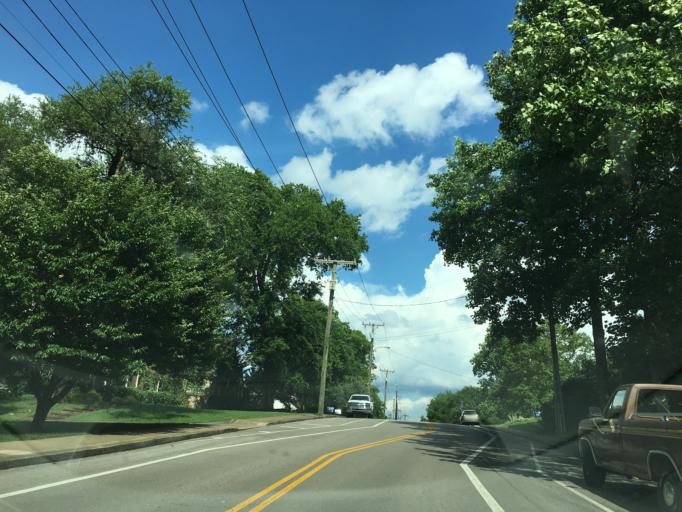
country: US
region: Tennessee
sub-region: Davidson County
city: Nashville
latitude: 36.1354
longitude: -86.8141
